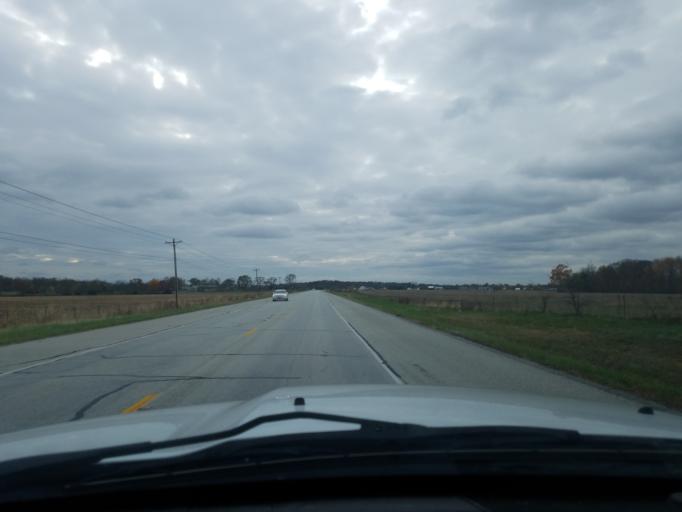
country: US
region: Indiana
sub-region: Bartholomew County
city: Hope
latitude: 39.1784
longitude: -85.7763
